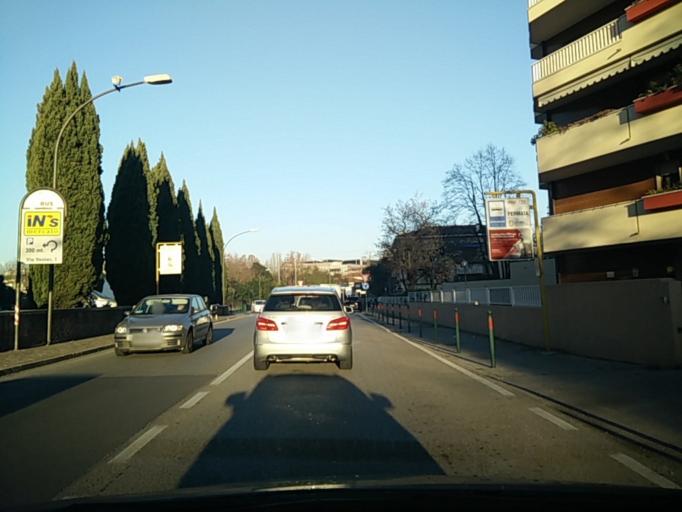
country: IT
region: Veneto
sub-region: Provincia di Treviso
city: Treviso
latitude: 45.6597
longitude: 12.2547
